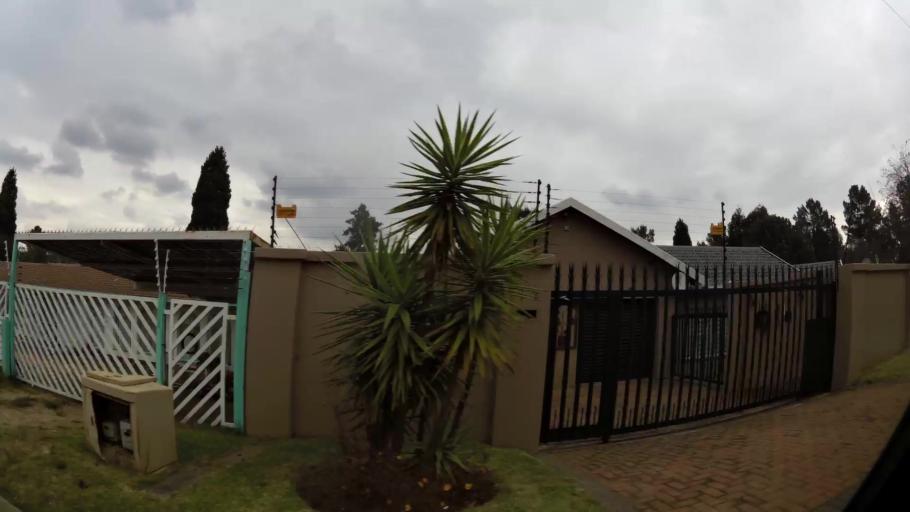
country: ZA
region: Gauteng
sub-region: City of Johannesburg Metropolitan Municipality
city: Roodepoort
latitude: -26.1113
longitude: 27.9064
